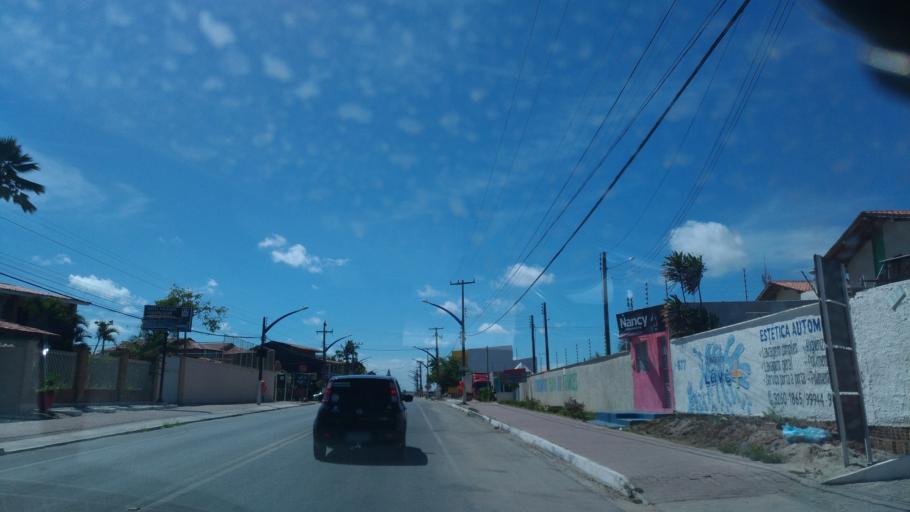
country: BR
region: Alagoas
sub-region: Marechal Deodoro
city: Marechal Deodoro
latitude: -9.7695
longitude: -35.8448
